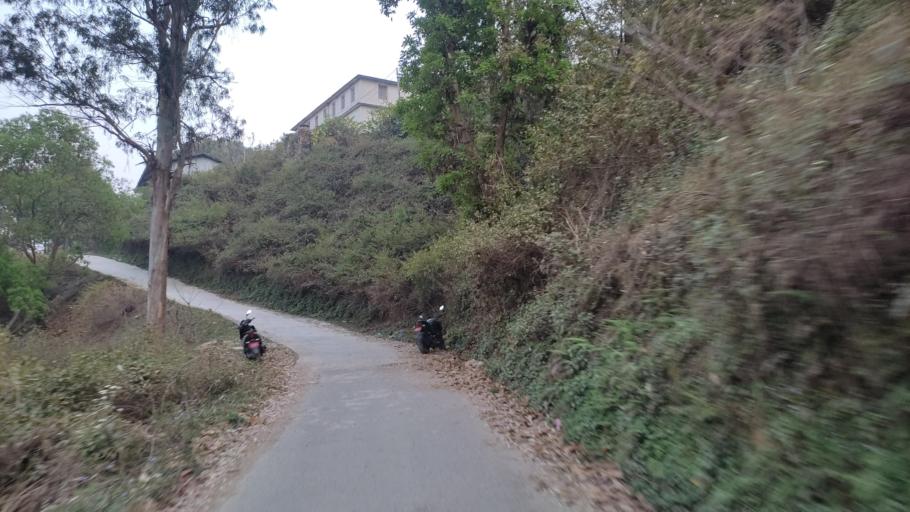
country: NP
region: Central Region
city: Kirtipur
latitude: 27.6675
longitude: 85.2927
